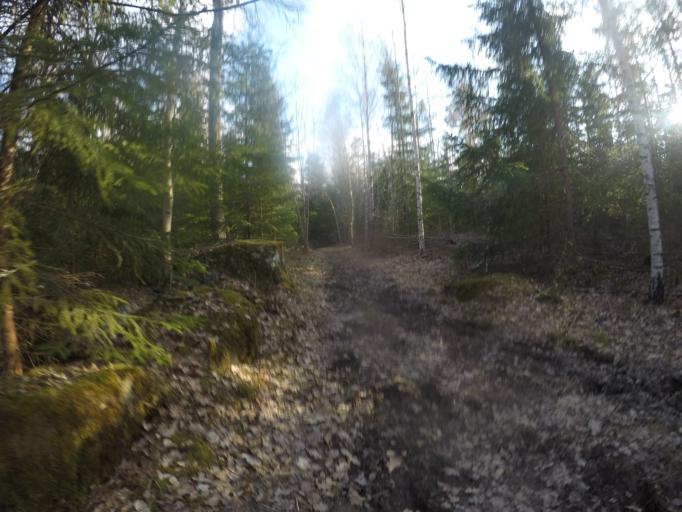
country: SE
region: Soedermanland
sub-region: Eskilstuna Kommun
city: Hallbybrunn
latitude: 59.3847
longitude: 16.4058
